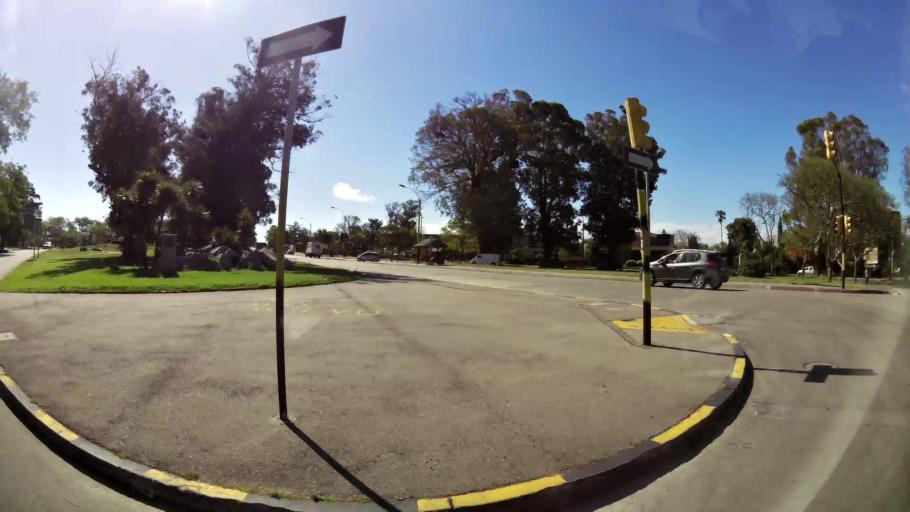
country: UY
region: Canelones
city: Paso de Carrasco
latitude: -34.8914
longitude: -56.0716
